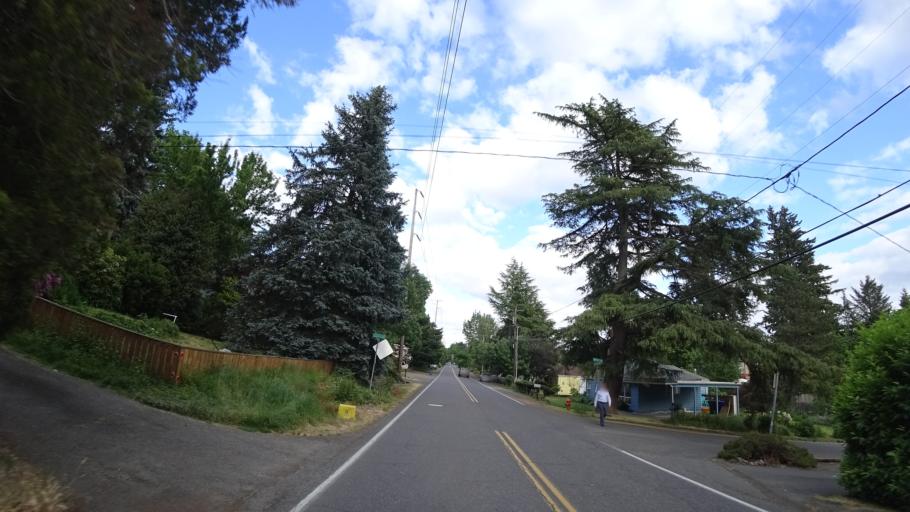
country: US
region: Oregon
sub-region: Washington County
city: Raleigh Hills
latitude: 45.4836
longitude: -122.7346
